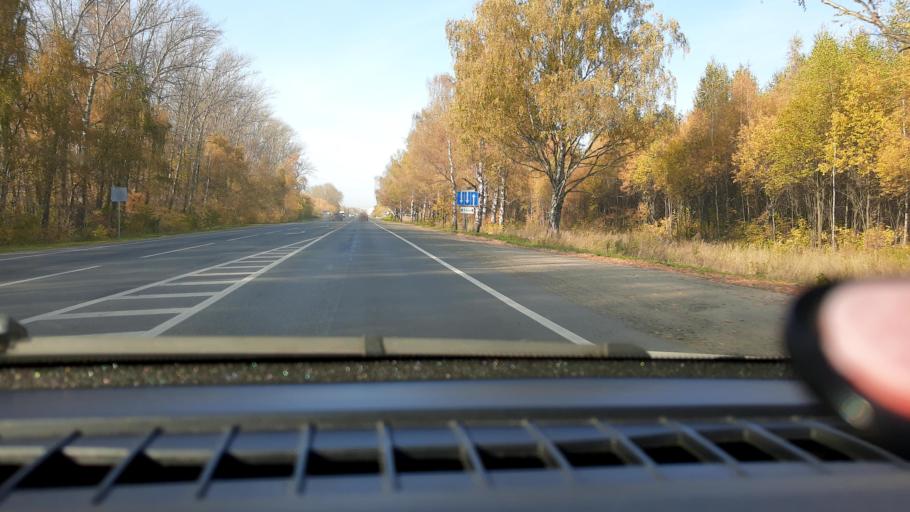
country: RU
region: Nizjnij Novgorod
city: Kstovo
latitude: 56.1391
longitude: 44.2328
